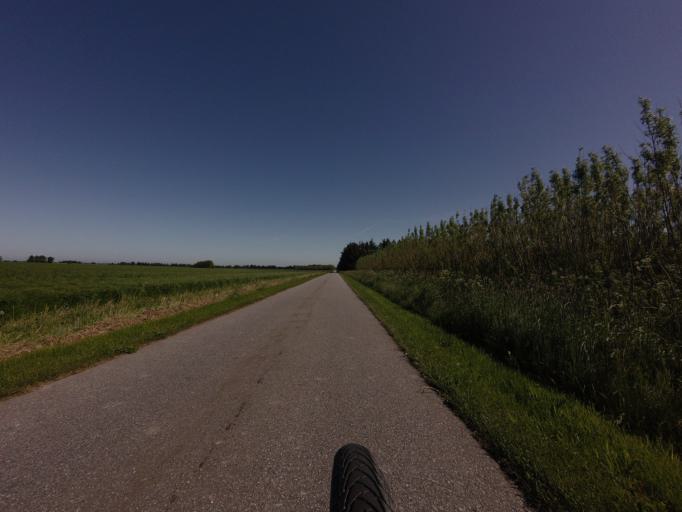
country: DK
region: North Denmark
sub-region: Hjorring Kommune
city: Vra
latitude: 57.3735
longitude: 9.8125
